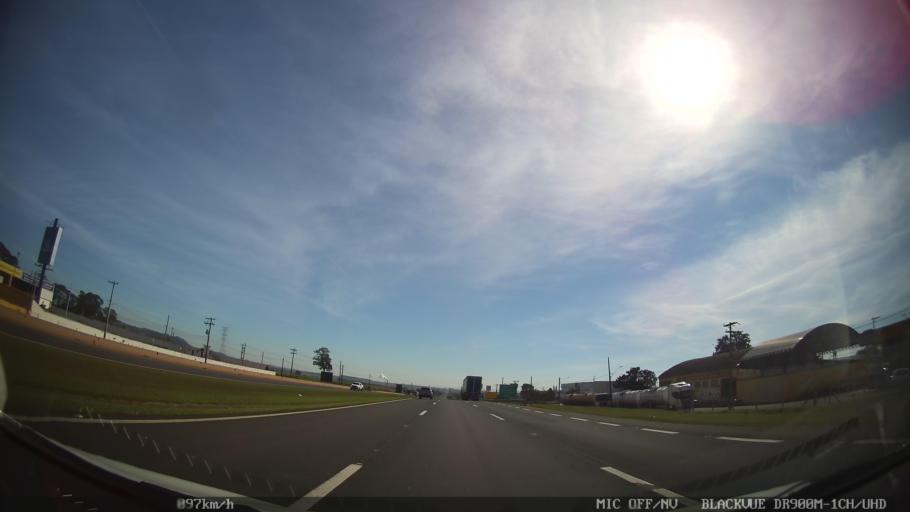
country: BR
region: Sao Paulo
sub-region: Pirassununga
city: Pirassununga
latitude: -22.0348
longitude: -47.4332
